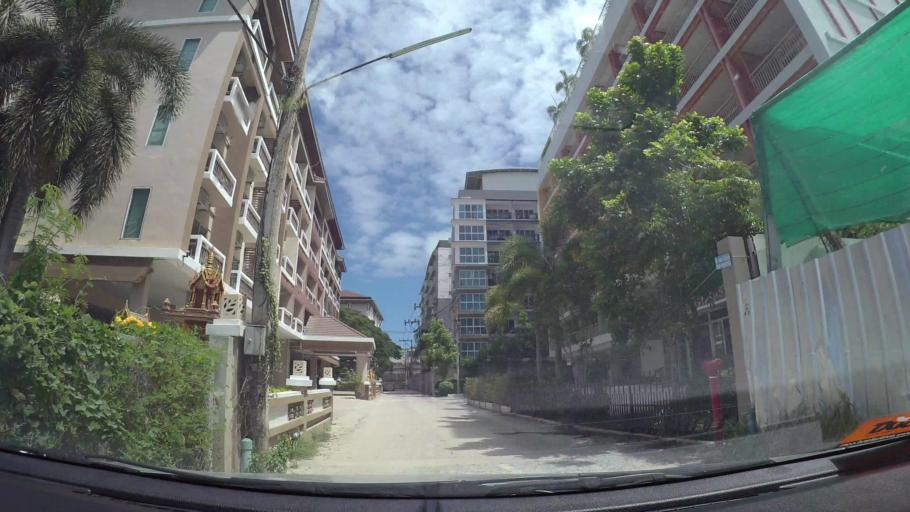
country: TH
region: Chon Buri
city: Phatthaya
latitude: 12.9270
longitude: 100.8810
